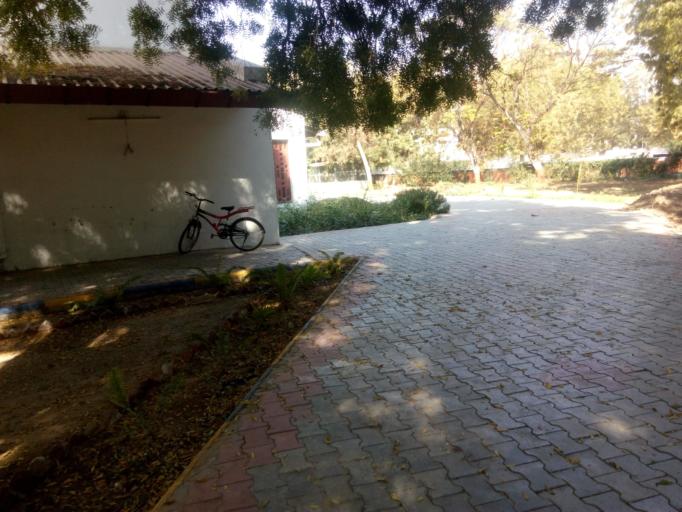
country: IN
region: Gujarat
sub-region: Ahmadabad
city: Ahmedabad
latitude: 23.0441
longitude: 72.5686
